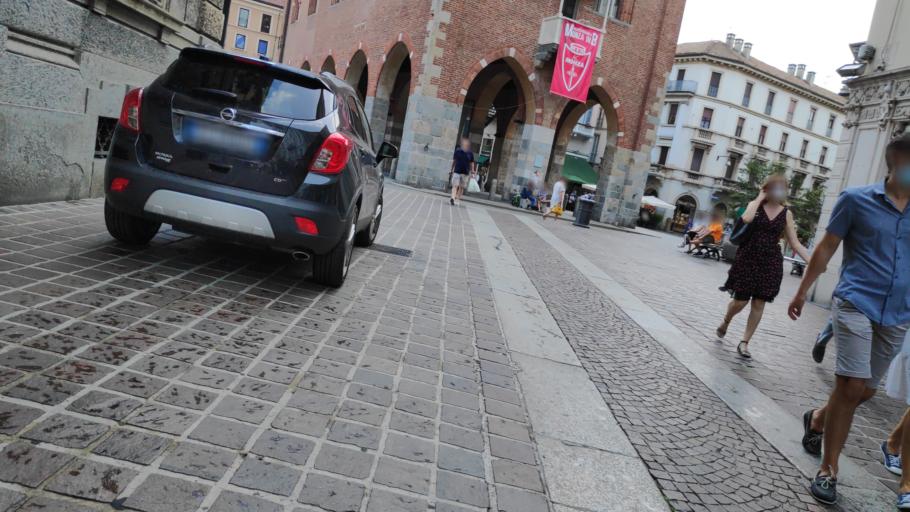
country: IT
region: Lombardy
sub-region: Provincia di Monza e Brianza
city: Monza
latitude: 45.5840
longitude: 9.2748
